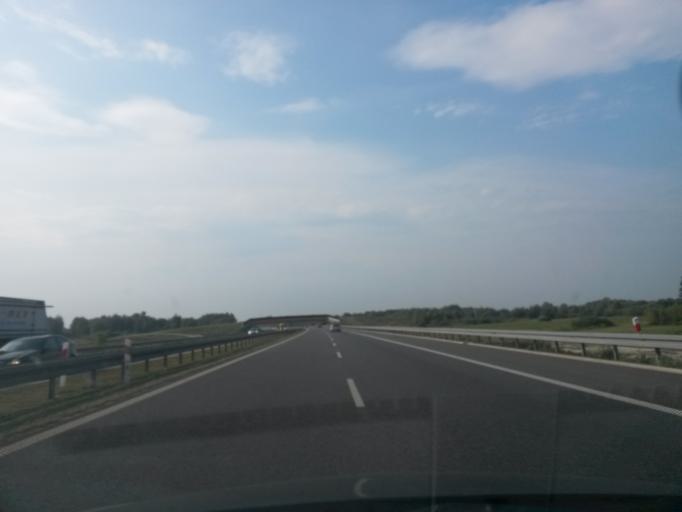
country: PL
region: Lesser Poland Voivodeship
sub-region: Powiat bochenski
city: Jodlowka
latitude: 50.0041
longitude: 20.5442
